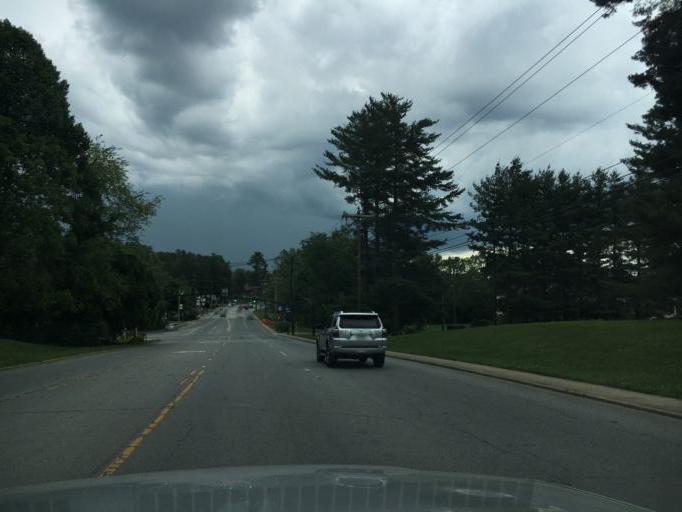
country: US
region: North Carolina
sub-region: Transylvania County
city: Brevard
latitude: 35.2380
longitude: -82.7310
